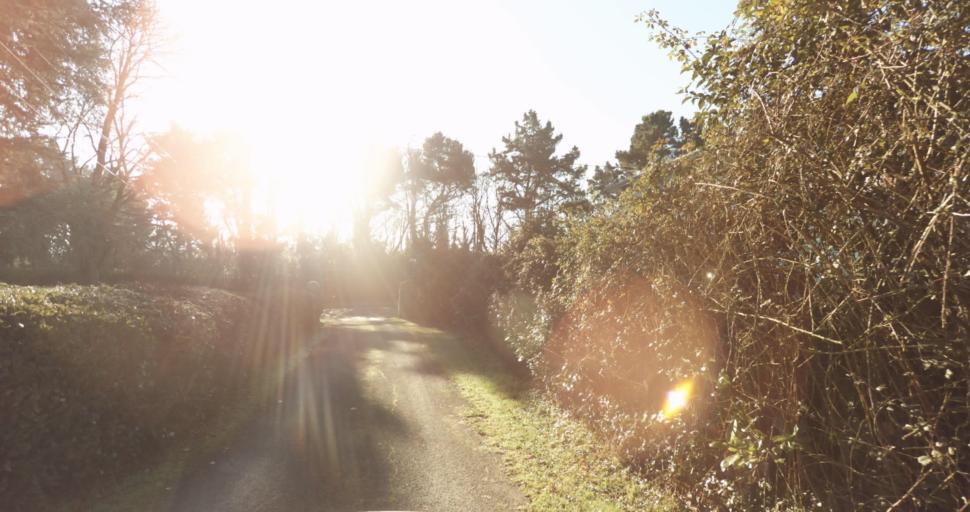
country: FR
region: Aquitaine
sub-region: Departement de la Gironde
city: Lormont
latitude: 44.8859
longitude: -0.5120
